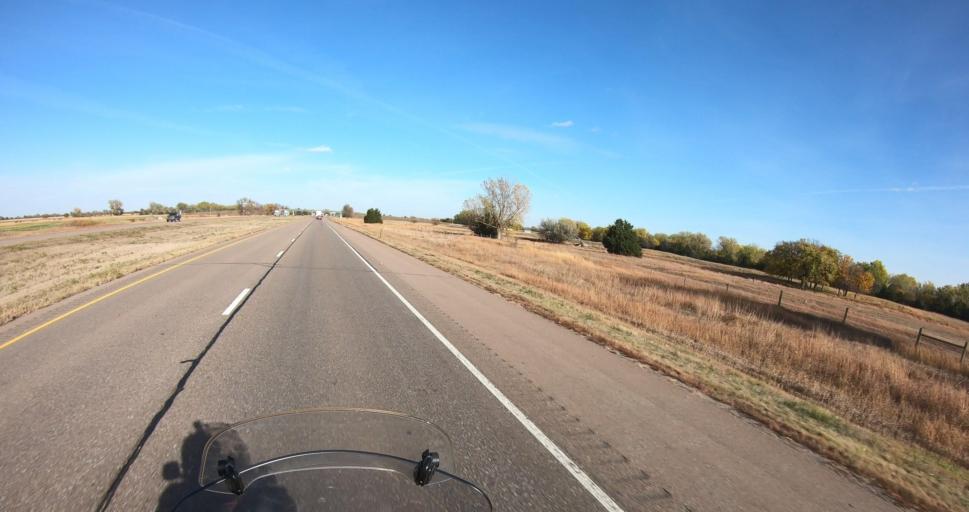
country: US
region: Nebraska
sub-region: Buffalo County
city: Gibbon
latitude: 40.7088
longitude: -98.8223
